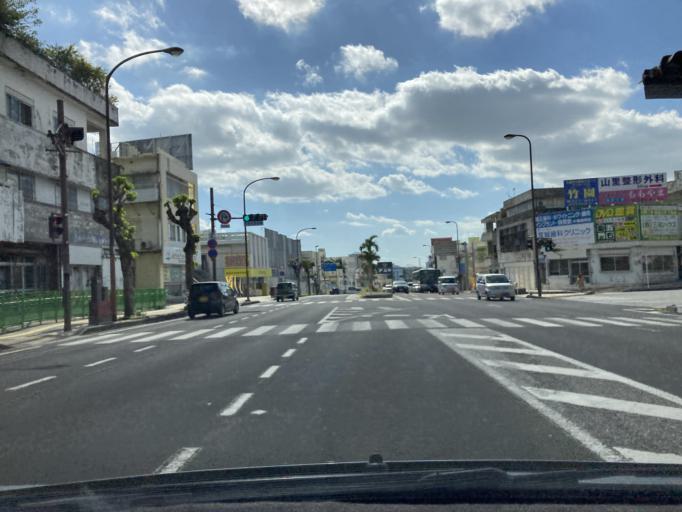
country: JP
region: Okinawa
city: Okinawa
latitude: 26.3238
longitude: 127.7931
